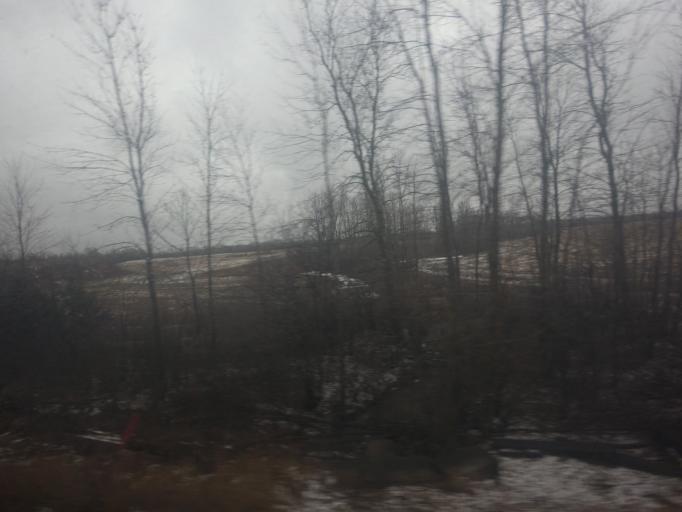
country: CA
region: Ontario
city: Deseronto
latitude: 44.2256
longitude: -77.0936
